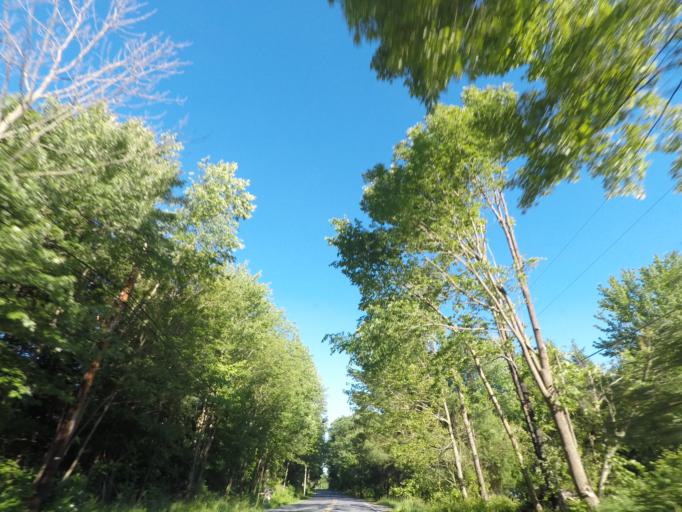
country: US
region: New York
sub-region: Rensselaer County
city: West Sand Lake
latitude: 42.5976
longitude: -73.5957
